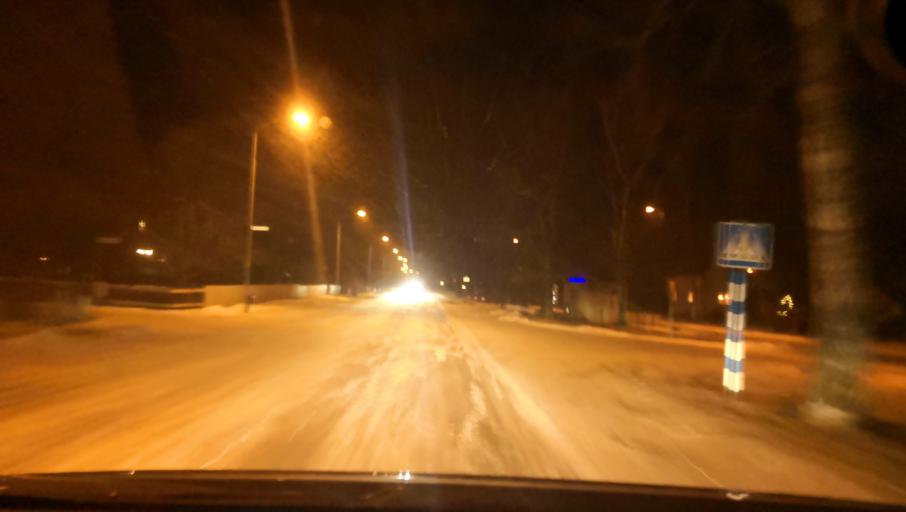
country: SE
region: Uppsala
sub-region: Heby Kommun
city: Tarnsjo
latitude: 60.1512
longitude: 16.9230
